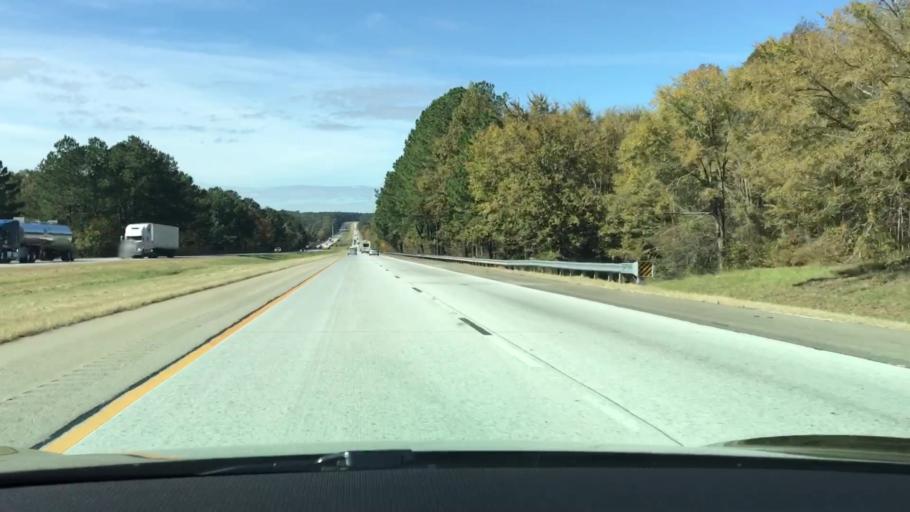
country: US
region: Georgia
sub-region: Greene County
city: Greensboro
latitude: 33.5350
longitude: -83.2614
